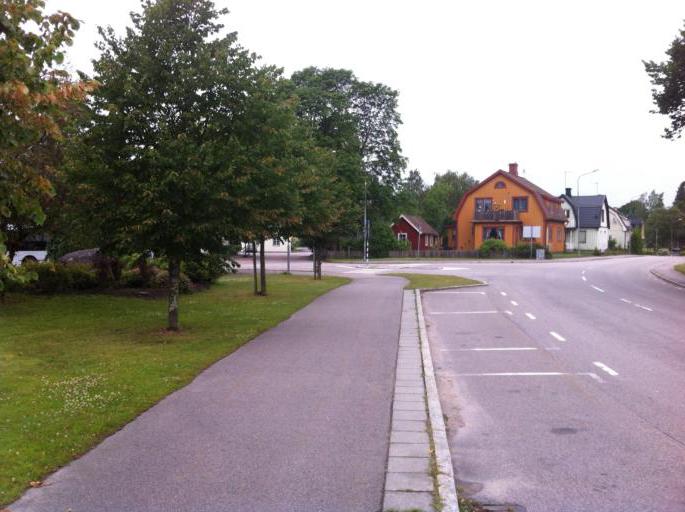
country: SE
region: Joenkoeping
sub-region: Gislaveds Kommun
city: Reftele
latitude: 56.9545
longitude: 13.5290
